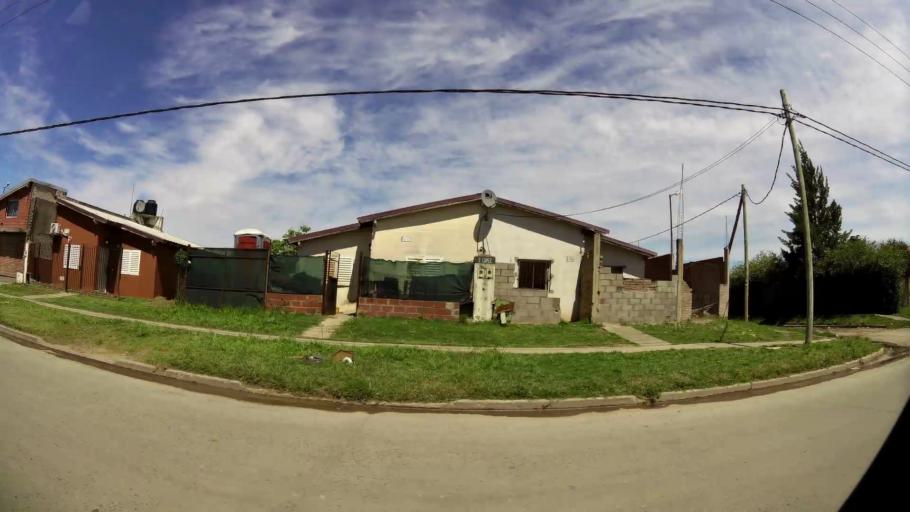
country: AR
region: Buenos Aires
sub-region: Partido de Quilmes
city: Quilmes
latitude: -34.7439
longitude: -58.3119
